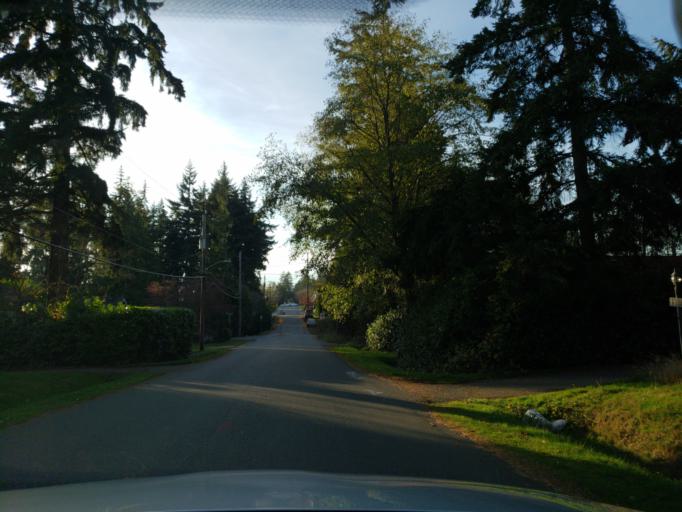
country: US
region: Washington
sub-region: King County
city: Shoreline
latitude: 47.7505
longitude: -122.3418
